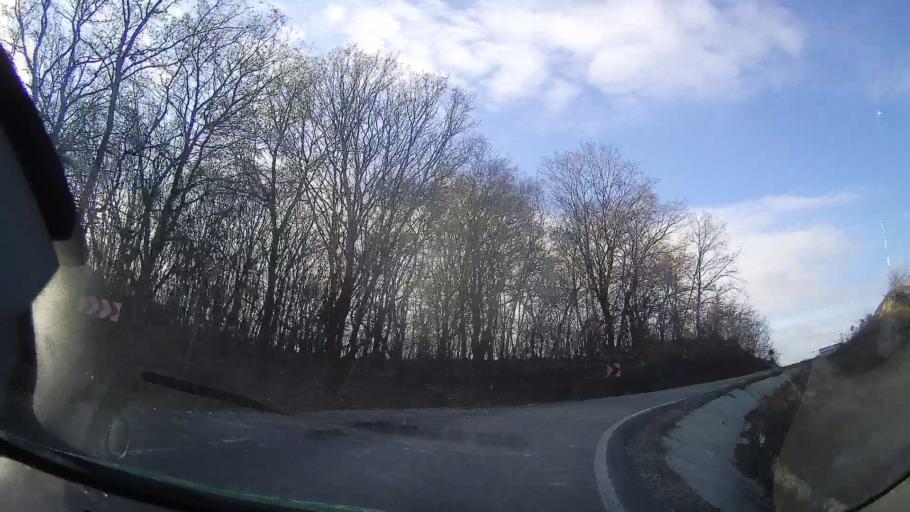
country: RO
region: Mures
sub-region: Comuna Papiu Ilarian
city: Papiu Ilarian
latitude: 46.5588
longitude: 24.1756
